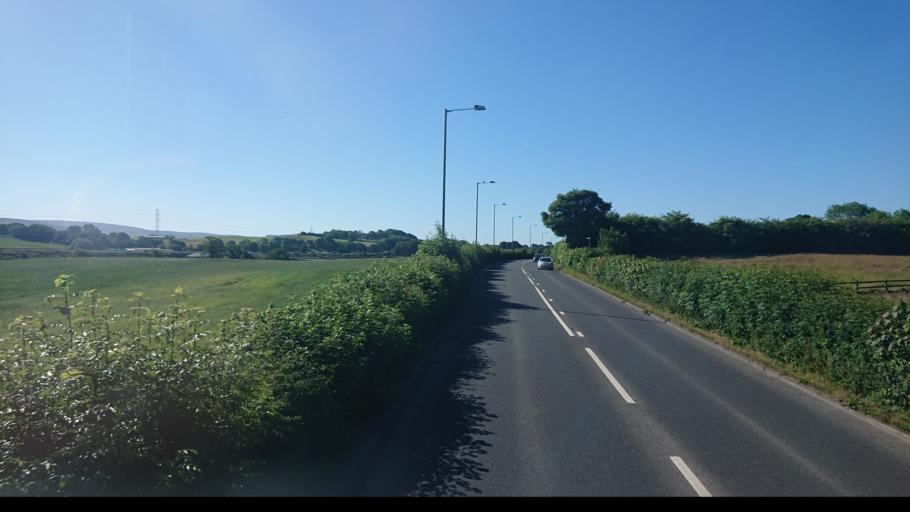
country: GB
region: England
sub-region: Lancashire
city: Bay Horse
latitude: 53.9647
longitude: -2.7777
